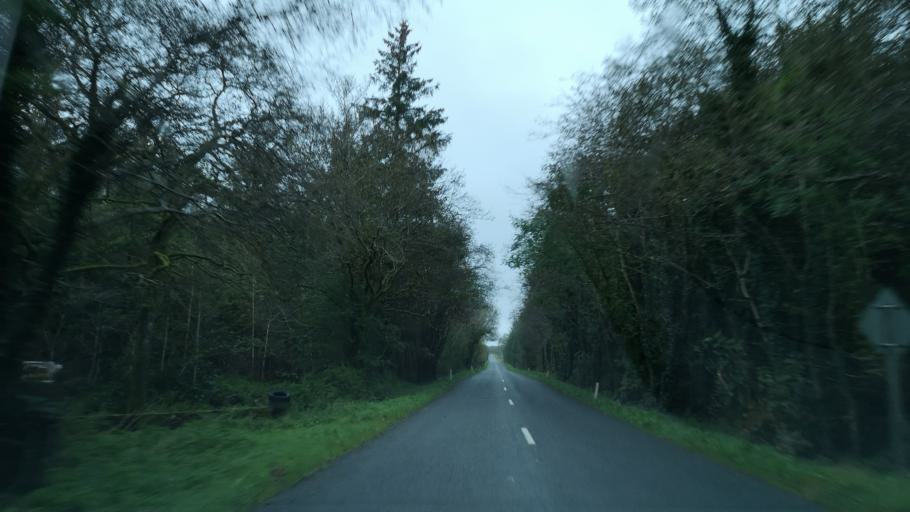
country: IE
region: Connaught
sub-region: Maigh Eo
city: Ballyhaunis
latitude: 53.7942
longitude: -8.7066
